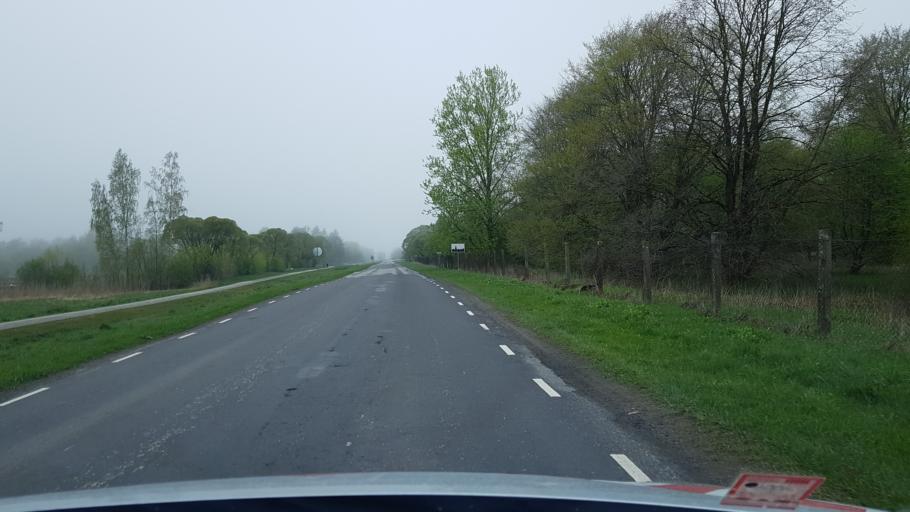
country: EE
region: Harju
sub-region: Joelaehtme vald
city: Loo
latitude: 59.4282
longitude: 24.9440
